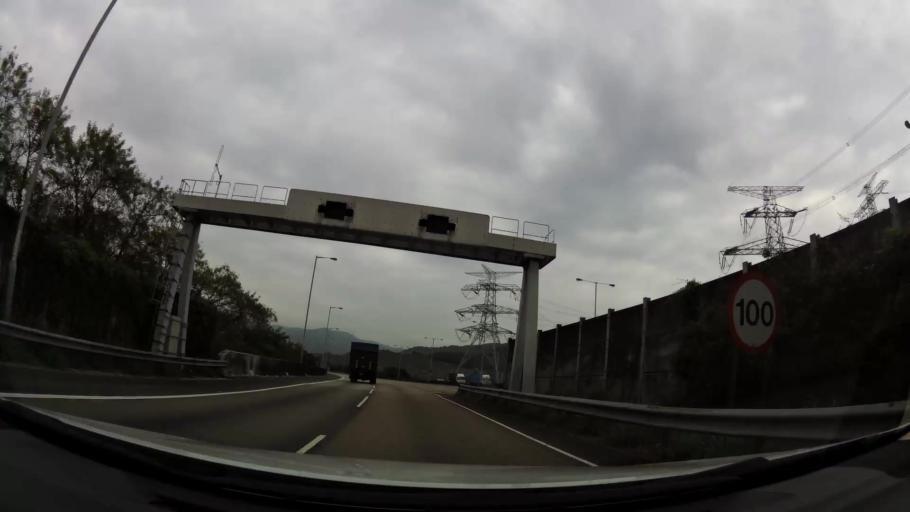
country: HK
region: Yuen Long
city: Yuen Long Kau Hui
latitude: 22.4432
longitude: 114.0512
